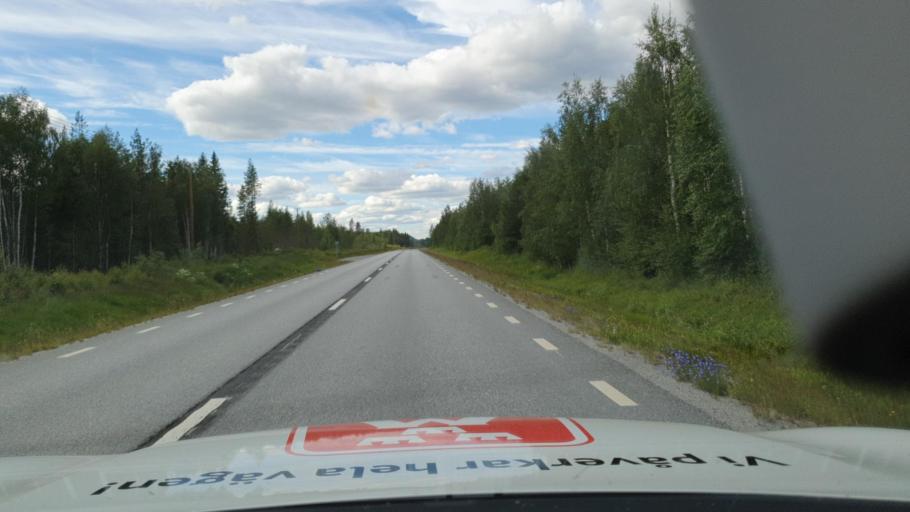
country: SE
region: Vaesterbotten
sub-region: Asele Kommun
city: Insjon
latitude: 64.1745
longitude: 17.7958
